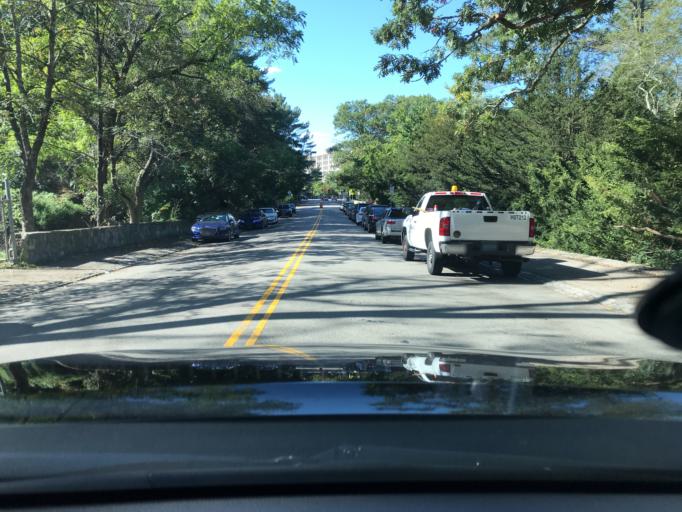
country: US
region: Massachusetts
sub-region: Suffolk County
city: Jamaica Plain
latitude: 42.2963
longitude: -71.1266
